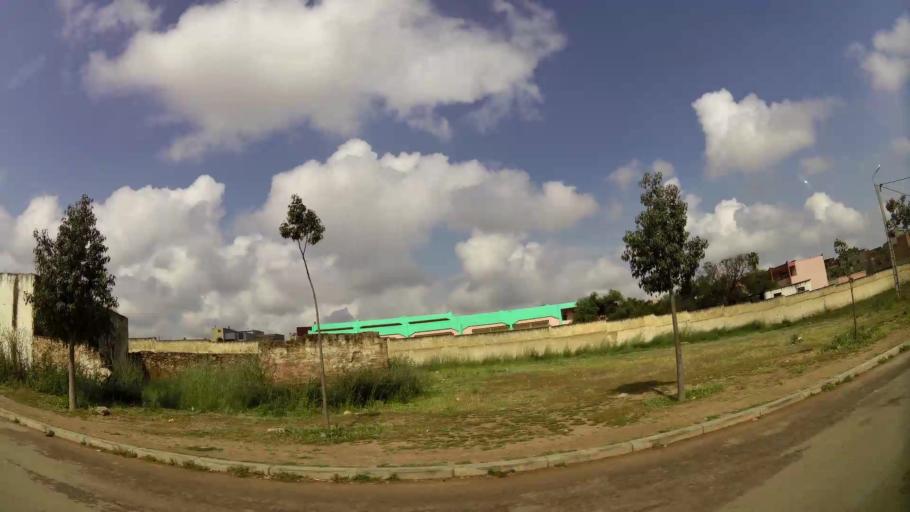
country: MA
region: Rabat-Sale-Zemmour-Zaer
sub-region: Khemisset
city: Tiflet
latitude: 33.8952
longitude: -6.3235
